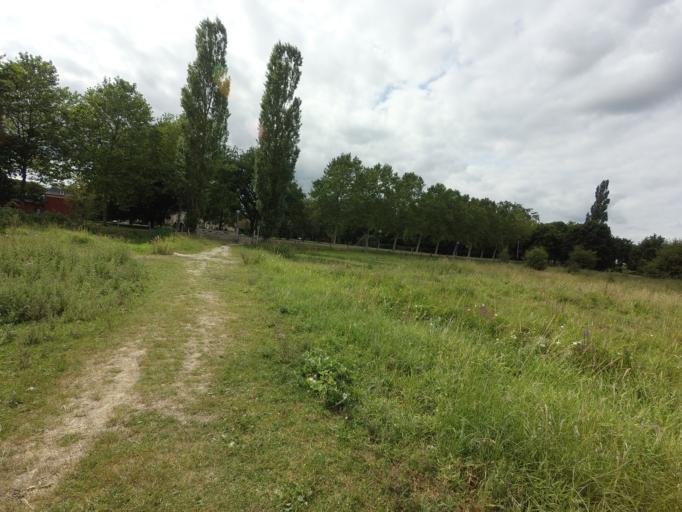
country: NL
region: Limburg
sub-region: Valkenburg aan de Geul
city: Houthem
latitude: 50.8698
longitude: 5.8014
